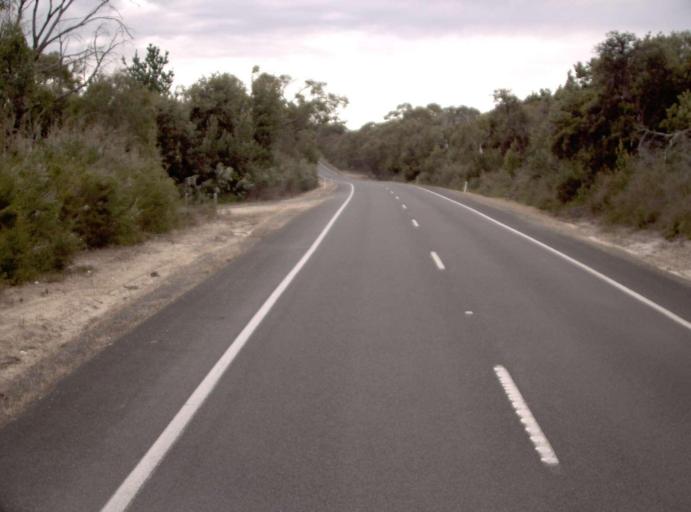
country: AU
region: Victoria
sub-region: Wellington
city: Sale
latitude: -38.2562
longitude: 147.0421
